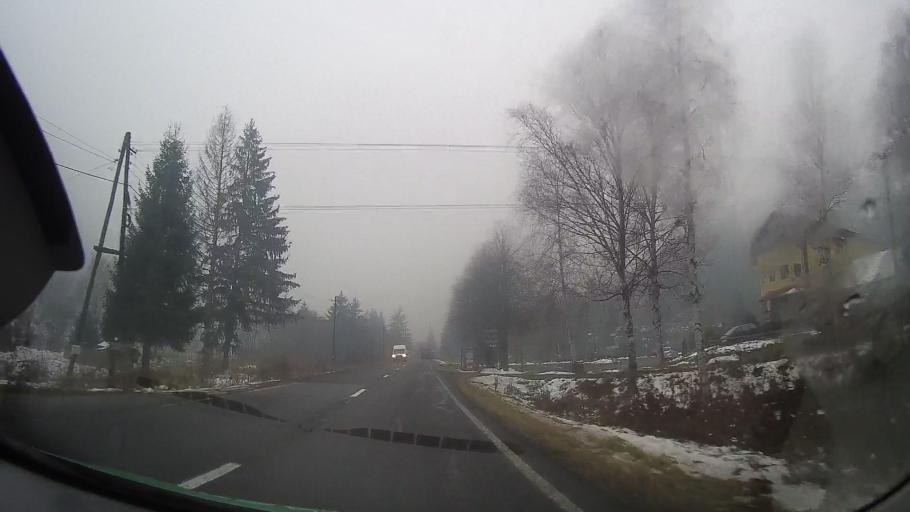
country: RO
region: Harghita
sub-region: Municipiul Gheorgheni
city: Gheorgheni
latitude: 46.7455
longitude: 25.6751
